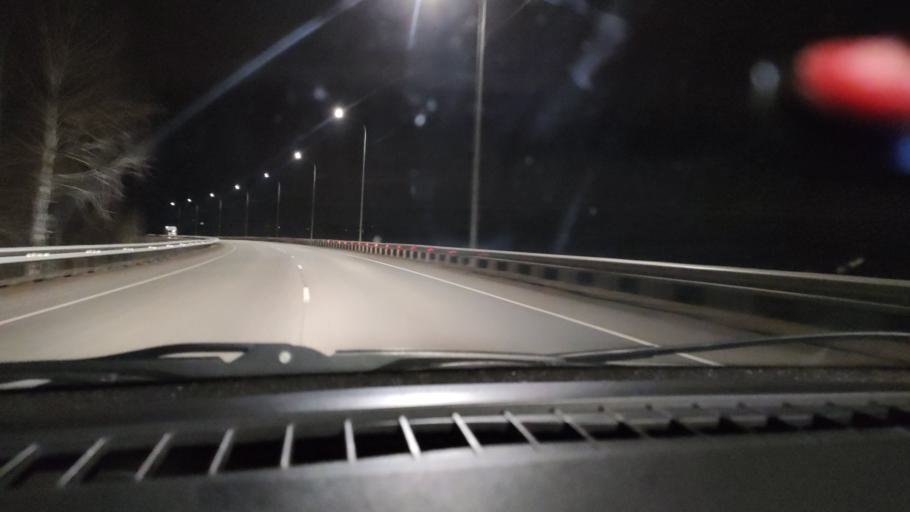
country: RU
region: Bashkortostan
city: Yermolayevo
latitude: 52.6527
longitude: 55.8372
